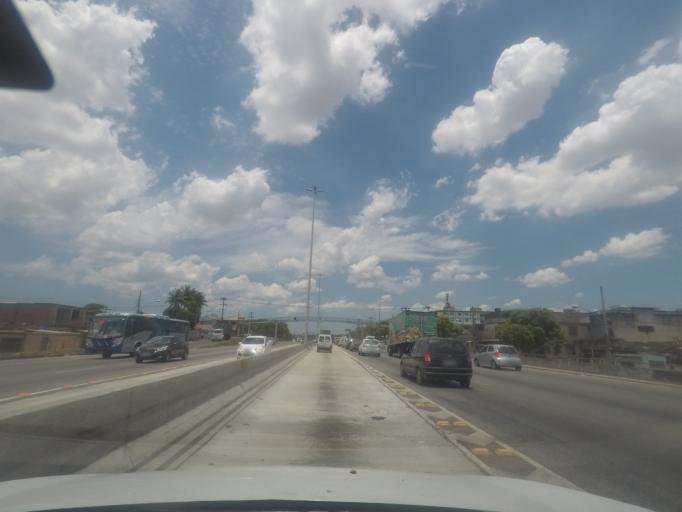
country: BR
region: Rio de Janeiro
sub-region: Sao Joao De Meriti
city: Sao Joao de Meriti
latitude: -22.8305
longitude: -43.3496
